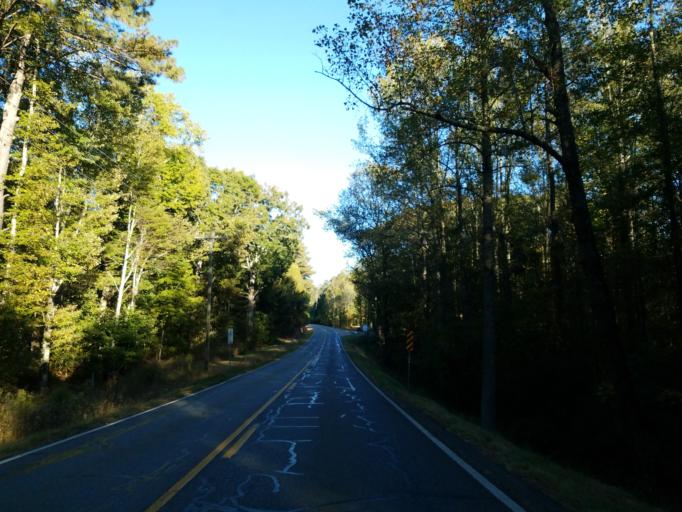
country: US
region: Georgia
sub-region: Pickens County
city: Nelson
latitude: 34.4141
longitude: -84.2745
